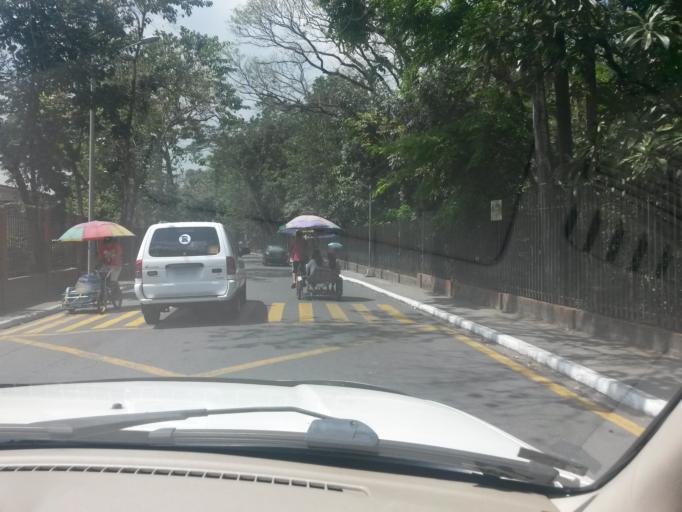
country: PH
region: Metro Manila
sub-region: Quezon City
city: Quezon City
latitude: 14.6535
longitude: 121.0759
